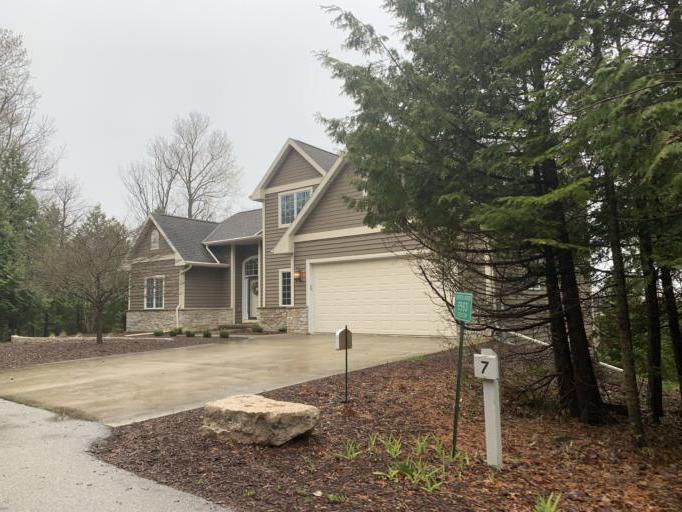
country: US
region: Wisconsin
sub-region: Door County
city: Sturgeon Bay
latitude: 45.0878
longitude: -87.2562
